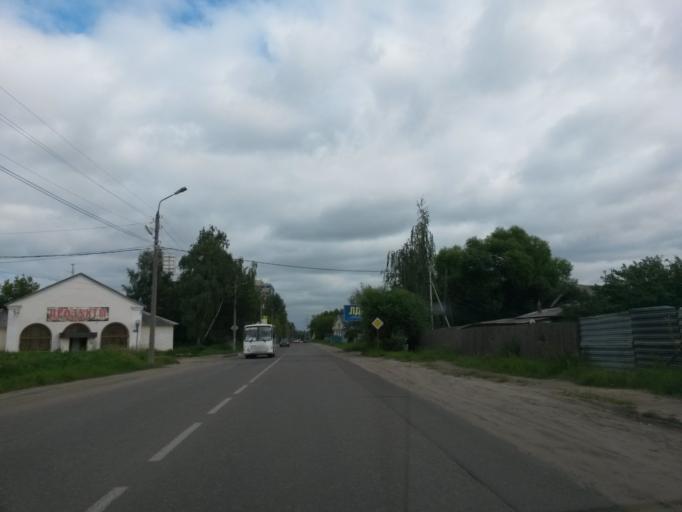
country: RU
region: Jaroslavl
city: Yaroslavl
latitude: 57.5810
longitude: 39.8709
